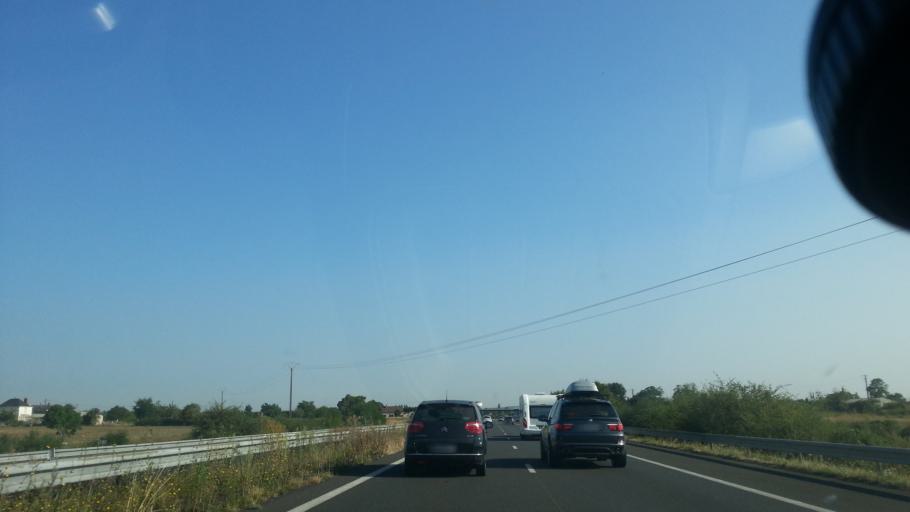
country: FR
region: Poitou-Charentes
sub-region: Departement de la Vienne
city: Chatellerault
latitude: 46.8094
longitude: 0.5139
